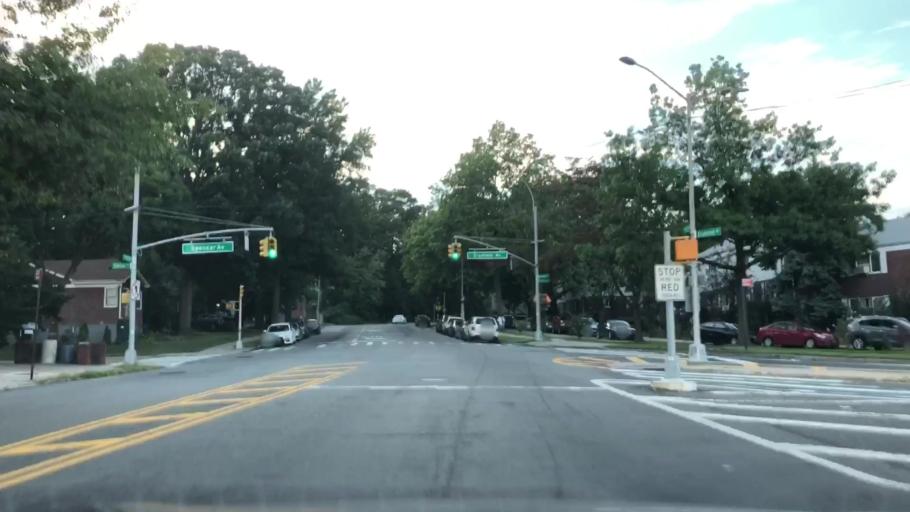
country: US
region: New York
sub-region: Nassau County
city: Bellerose Terrace
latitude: 40.7304
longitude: -73.7452
